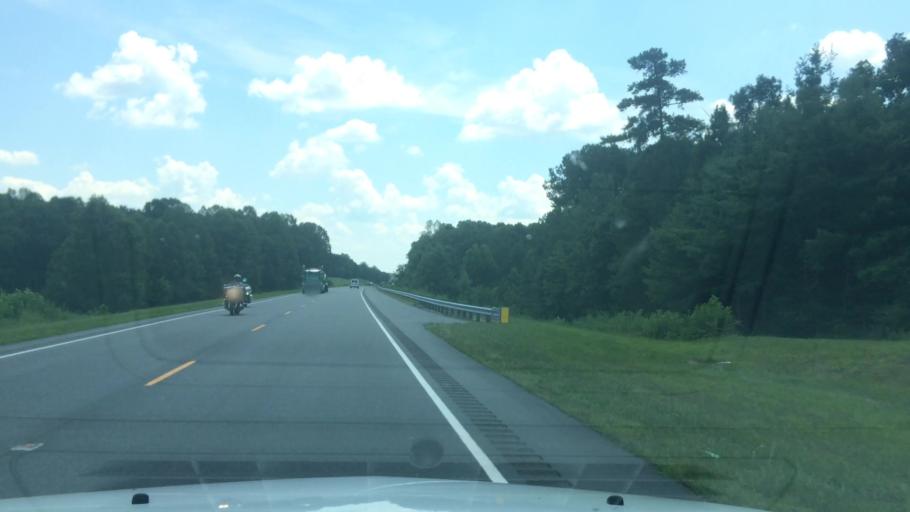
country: US
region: North Carolina
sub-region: Alexander County
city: Stony Point
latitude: 35.8757
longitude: -81.0686
